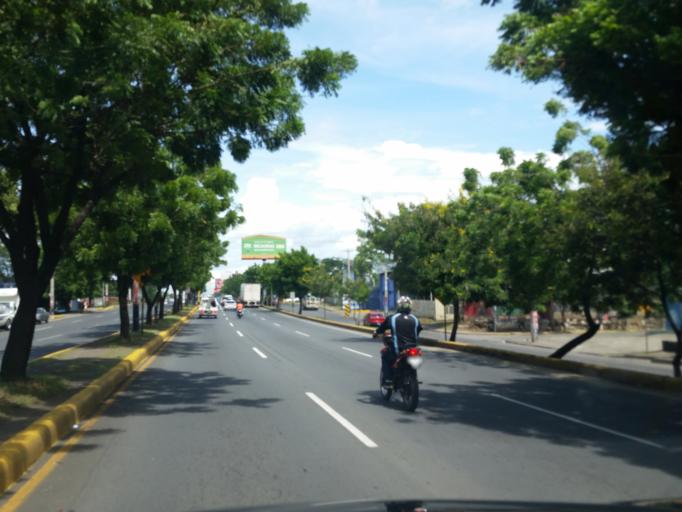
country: NI
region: Managua
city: Managua
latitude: 12.1499
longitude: -86.2165
